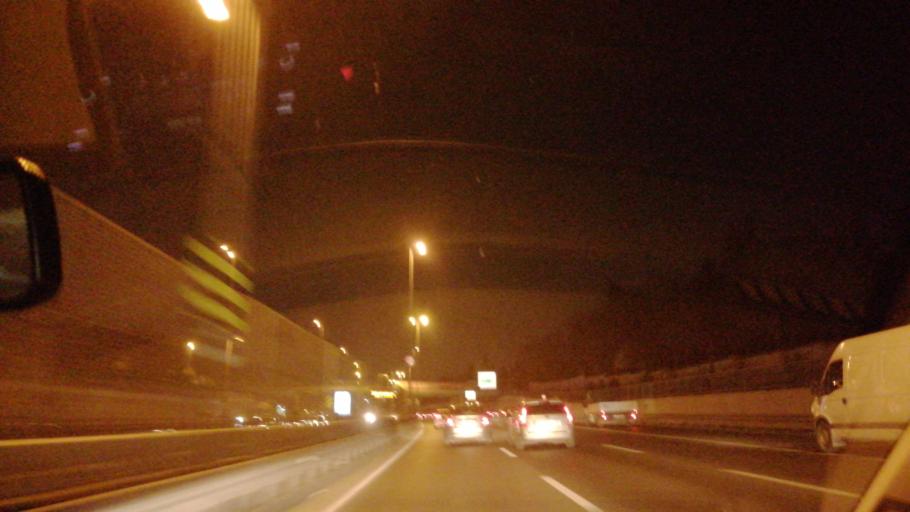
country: TR
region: Istanbul
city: Istanbul
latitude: 41.0229
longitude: 28.9207
